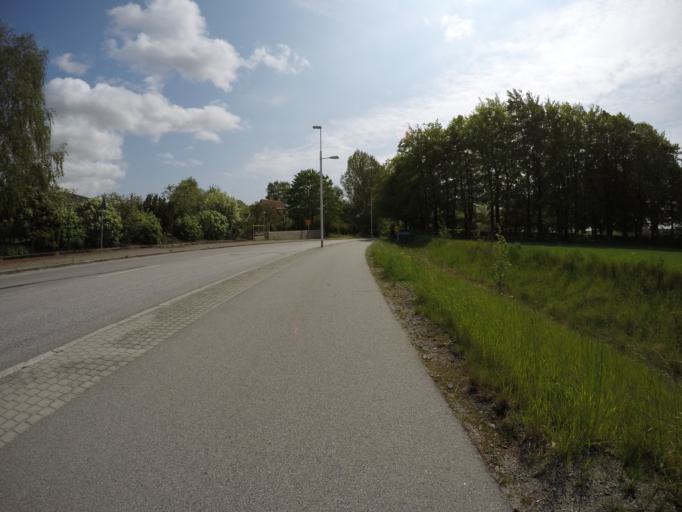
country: SE
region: Skane
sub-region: Malmo
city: Tygelsjo
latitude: 55.5298
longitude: 12.9956
